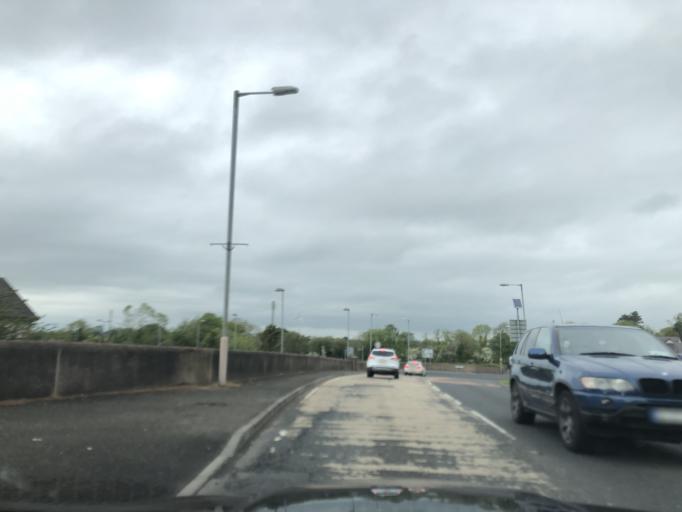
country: GB
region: Northern Ireland
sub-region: Antrim Borough
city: Templepatrick
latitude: 54.6141
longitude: -6.1203
